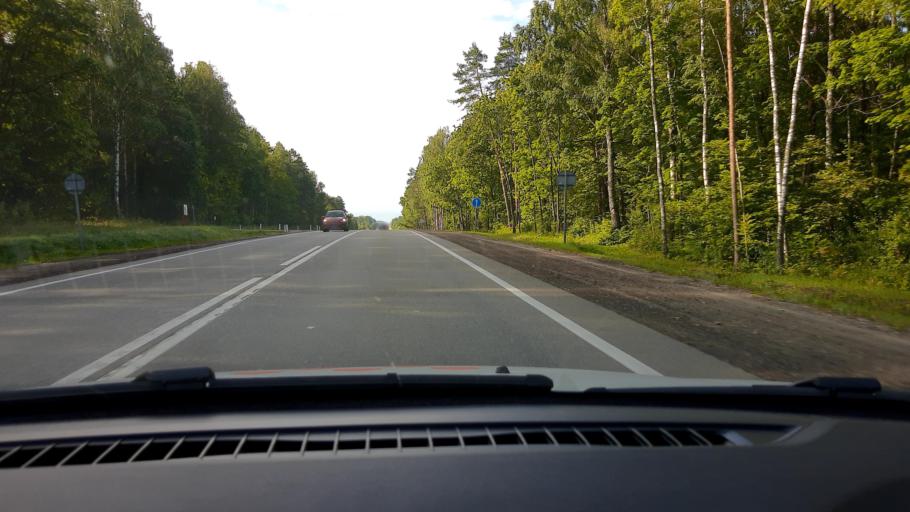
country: RU
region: Nizjnij Novgorod
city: Surovatikha
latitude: 55.7327
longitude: 43.9883
